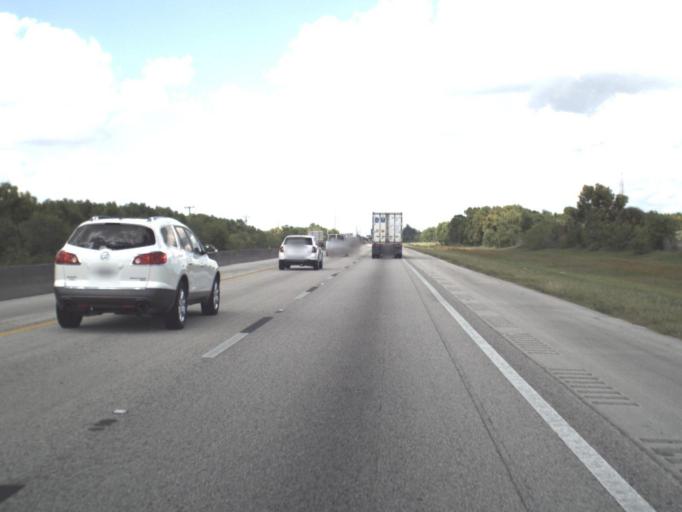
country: US
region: Florida
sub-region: Saint Lucie County
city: White City
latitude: 27.3633
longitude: -80.3784
